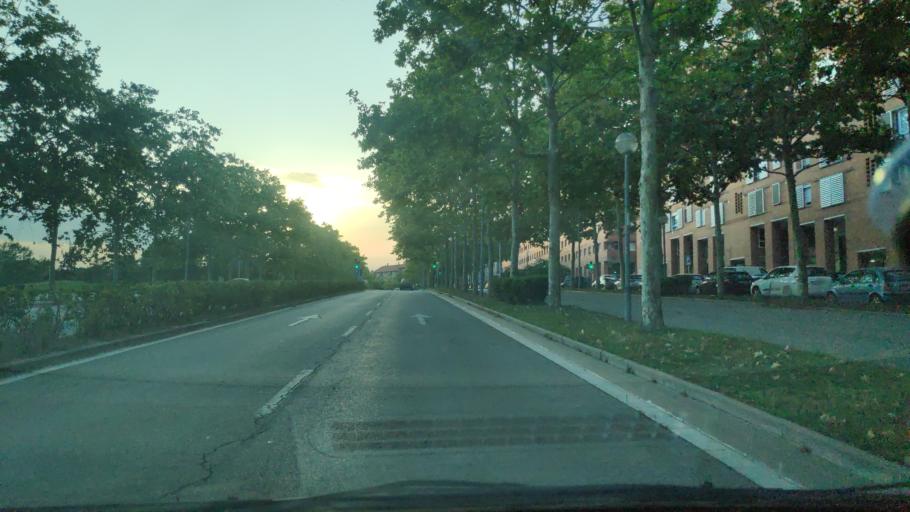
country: ES
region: Catalonia
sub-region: Provincia de Barcelona
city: Cerdanyola del Valles
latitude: 41.4833
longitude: 2.1527
